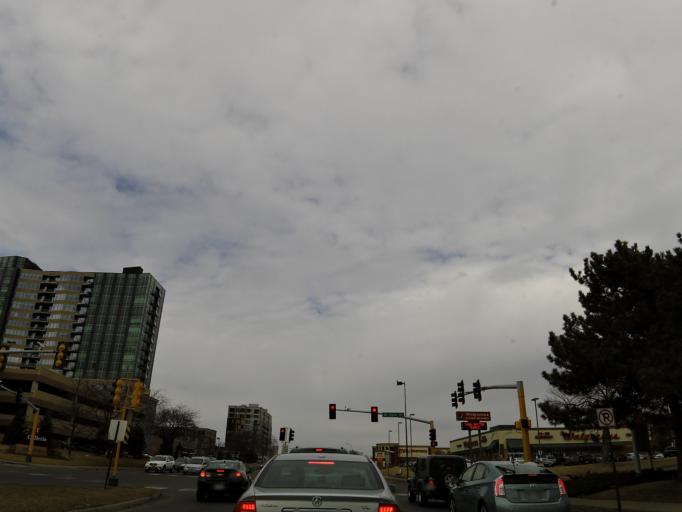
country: US
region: Minnesota
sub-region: Hennepin County
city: Edina
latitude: 44.8759
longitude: -93.3211
